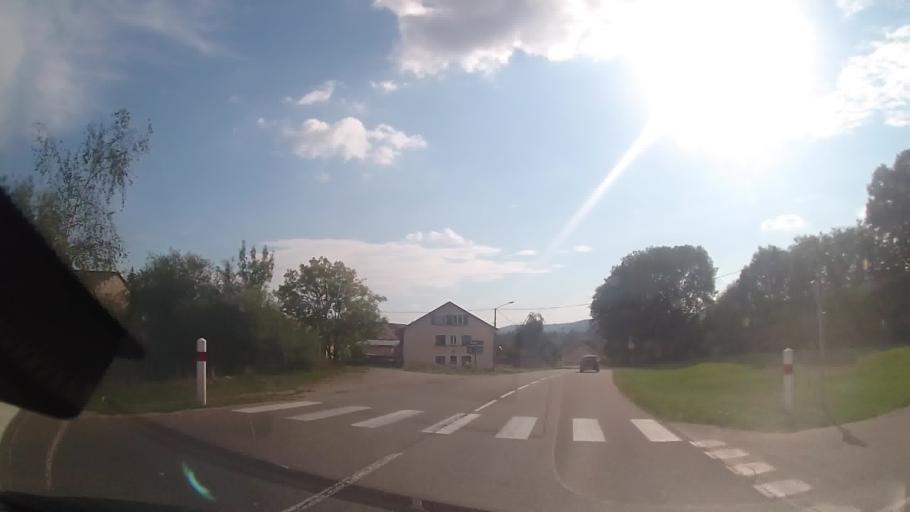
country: FR
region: Franche-Comte
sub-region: Departement du Jura
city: Clairvaux-les-Lacs
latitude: 46.5878
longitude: 5.7060
